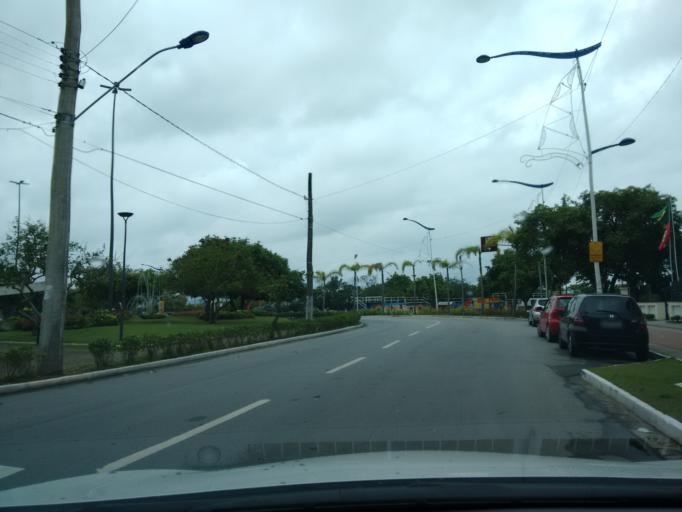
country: BR
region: Santa Catarina
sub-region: Itajai
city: Itajai
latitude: -26.9198
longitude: -48.6502
